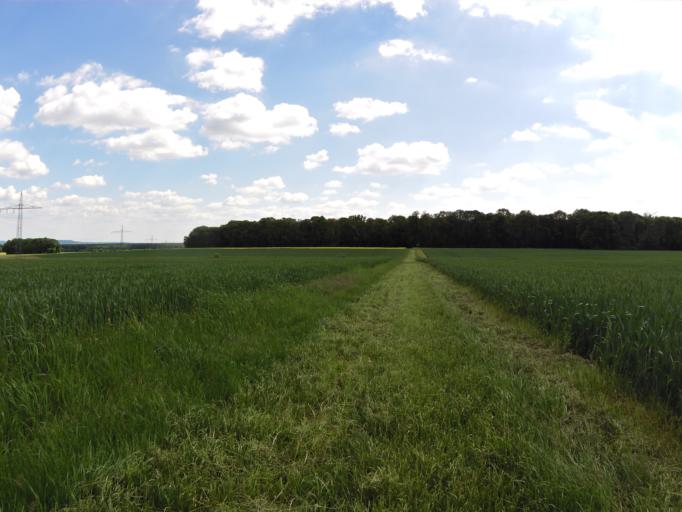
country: DE
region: Bavaria
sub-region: Regierungsbezirk Unterfranken
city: Theilheim
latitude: 49.7365
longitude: 10.0618
